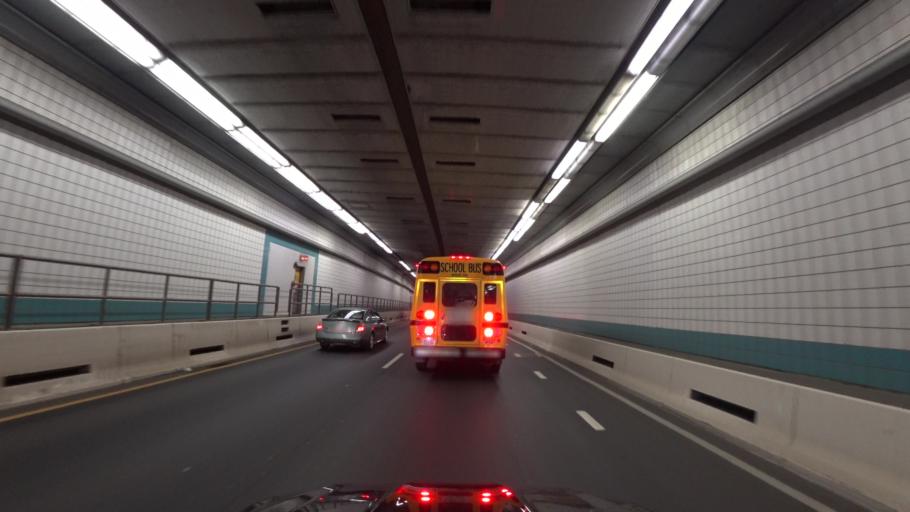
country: US
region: Massachusetts
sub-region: Suffolk County
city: South Boston
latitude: 42.3511
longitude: -71.0343
